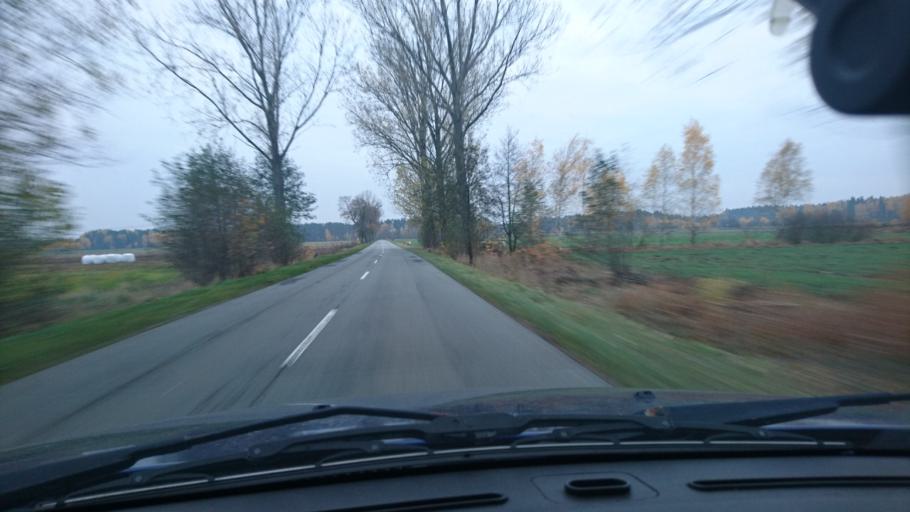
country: PL
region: Greater Poland Voivodeship
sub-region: Powiat ostrowski
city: Odolanow
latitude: 51.5372
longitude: 17.6508
